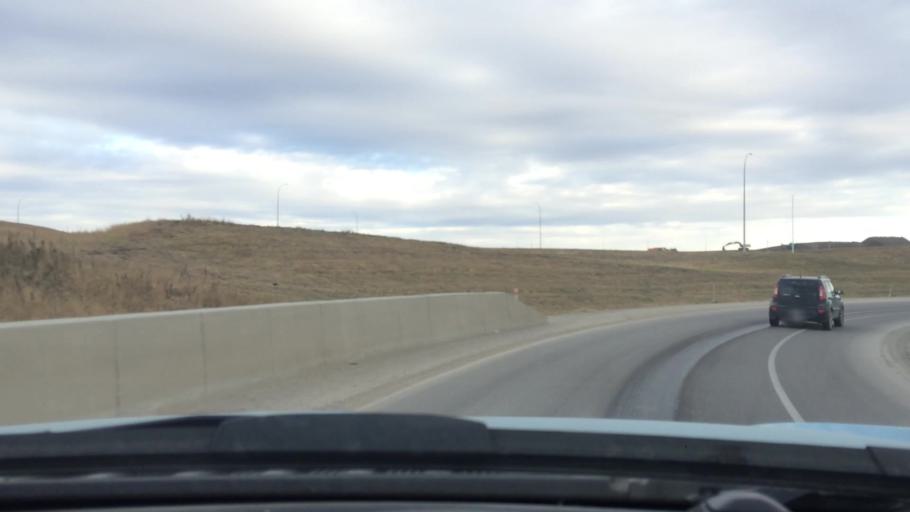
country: CA
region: Alberta
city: Calgary
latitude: 51.1503
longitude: -114.1689
